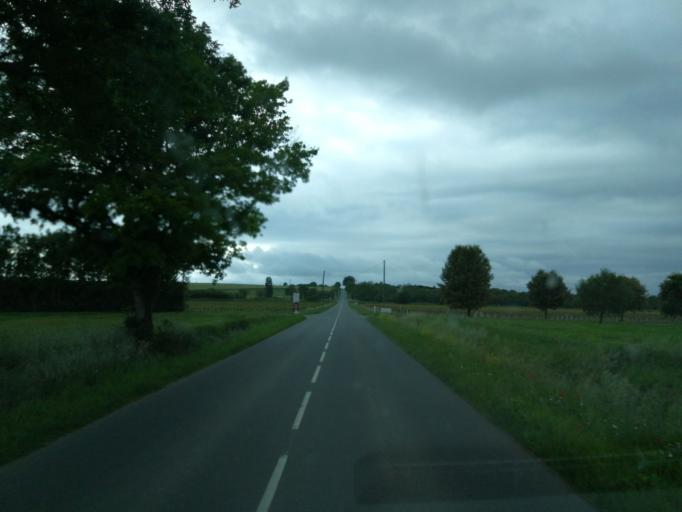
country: FR
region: Pays de la Loire
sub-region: Departement de la Vendee
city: Vix
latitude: 46.3717
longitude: -0.8975
